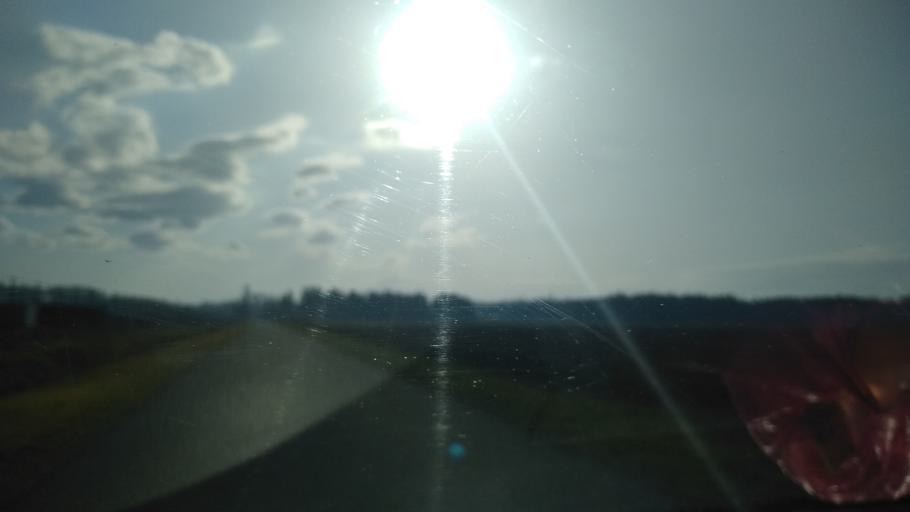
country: HU
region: Somogy
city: Barcs
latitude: 45.9689
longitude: 17.4976
